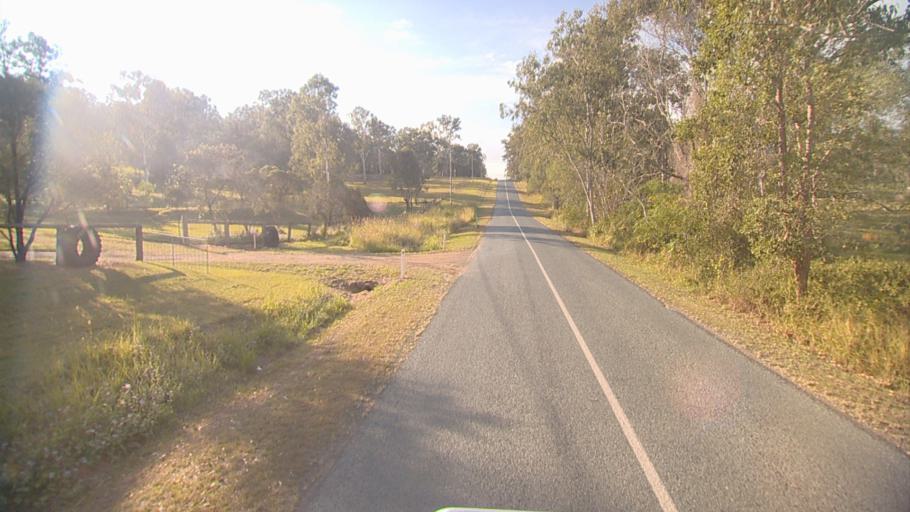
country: AU
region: Queensland
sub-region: Gold Coast
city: Ormeau Hills
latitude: -27.8369
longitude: 153.1687
